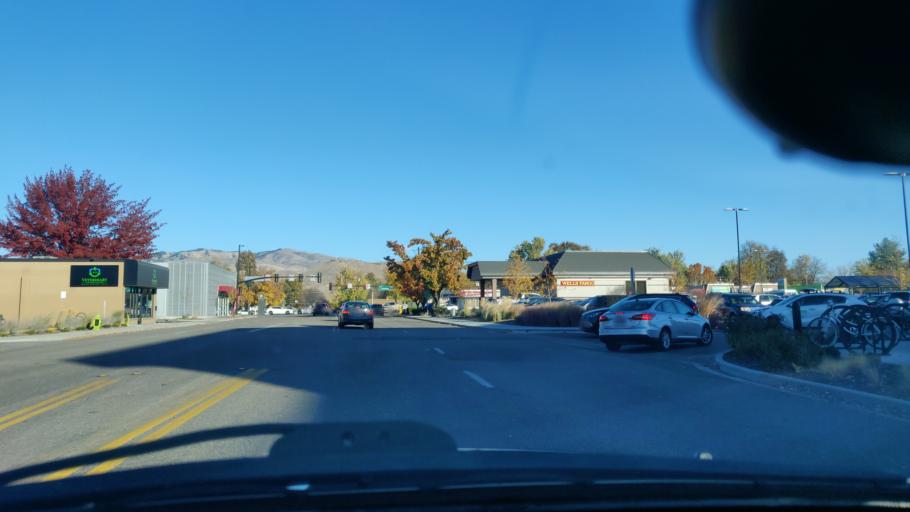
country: US
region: Idaho
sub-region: Ada County
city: Boise
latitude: 43.5984
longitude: -116.1952
